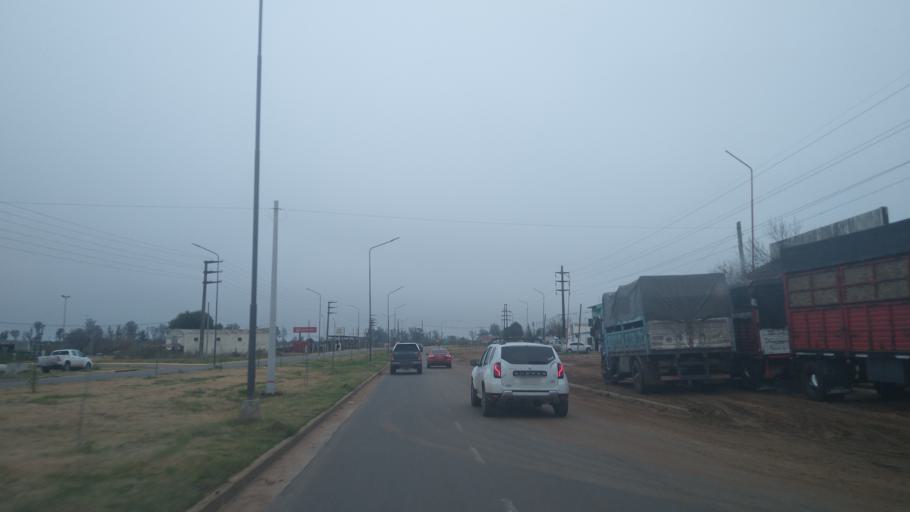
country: AR
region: Entre Rios
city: Chajari
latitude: -30.7620
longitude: -58.0119
